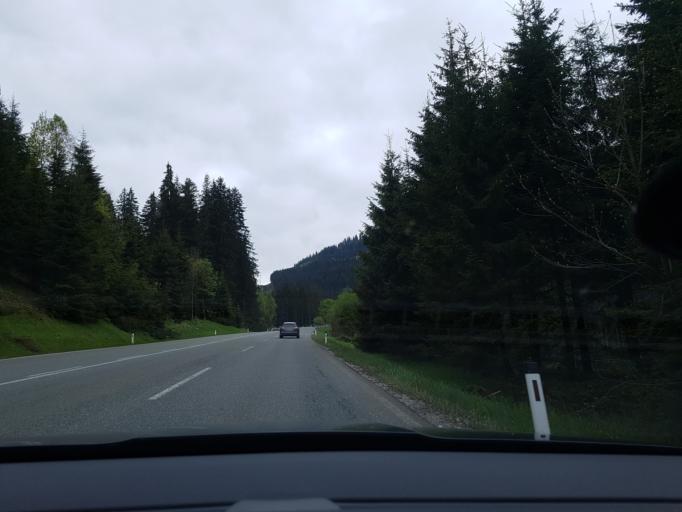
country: AT
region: Tyrol
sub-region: Politischer Bezirk Kitzbuhel
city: Jochberg
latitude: 47.3303
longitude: 12.4074
